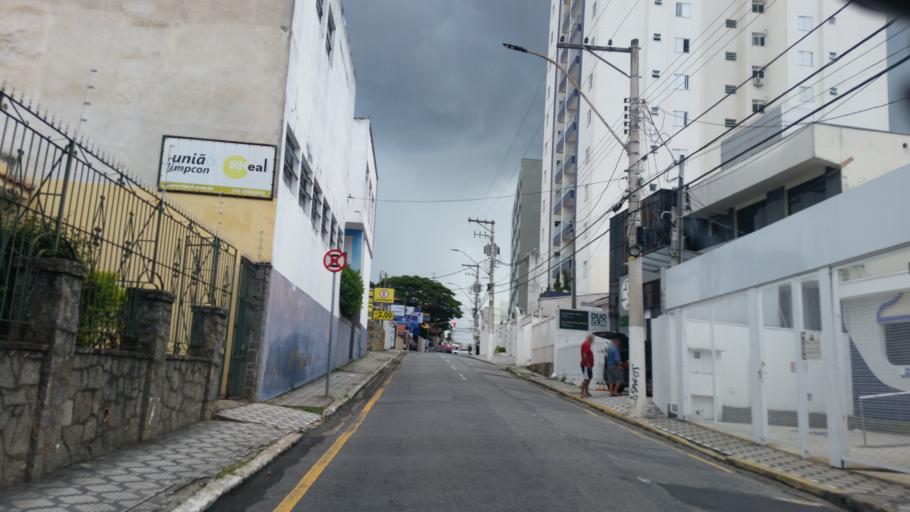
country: BR
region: Sao Paulo
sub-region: Taubate
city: Taubate
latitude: -23.0230
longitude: -45.5543
